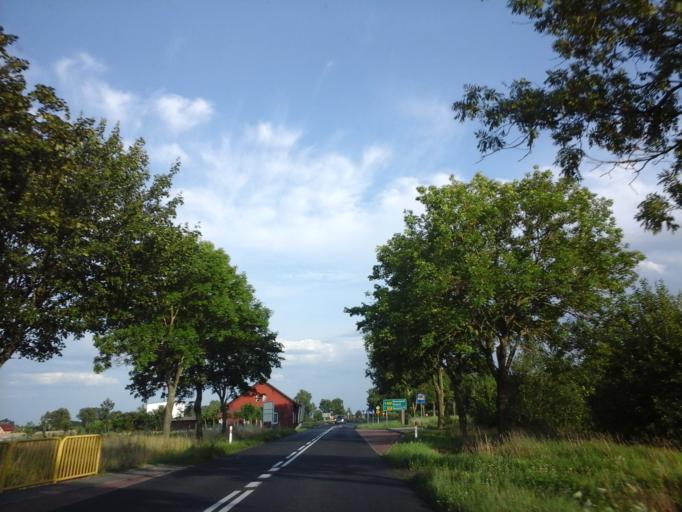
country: PL
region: West Pomeranian Voivodeship
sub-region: Powiat kamienski
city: Kamien Pomorski
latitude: 53.9394
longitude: 14.8132
